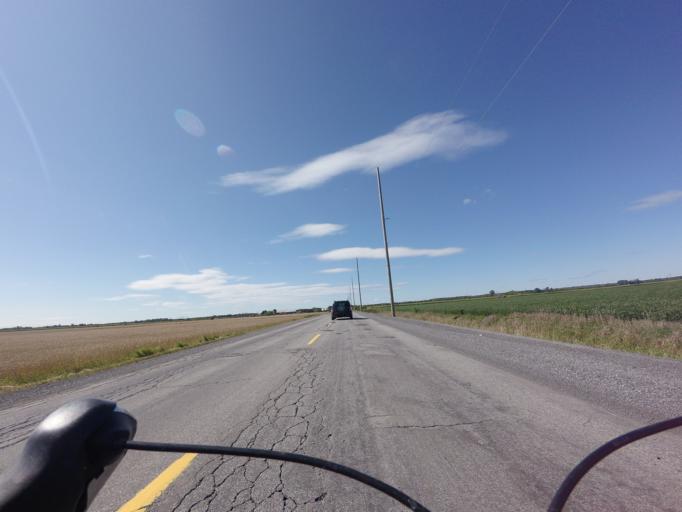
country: CA
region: Ontario
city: Bells Corners
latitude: 45.2424
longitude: -75.8648
